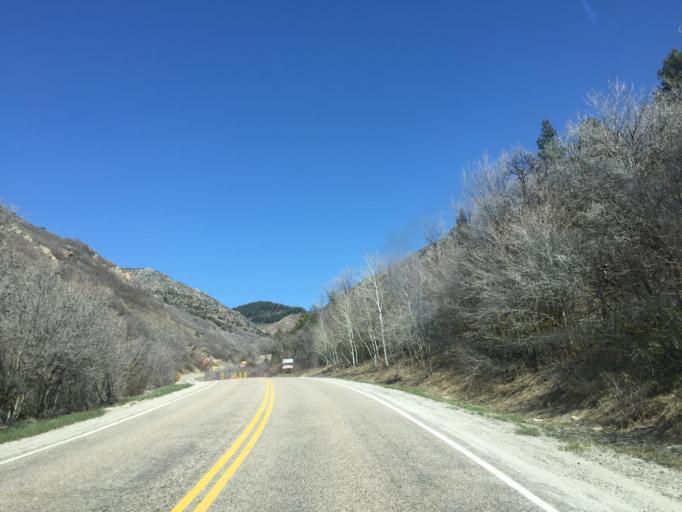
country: US
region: Utah
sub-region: Weber County
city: Wolf Creek
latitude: 41.3491
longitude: -111.8132
